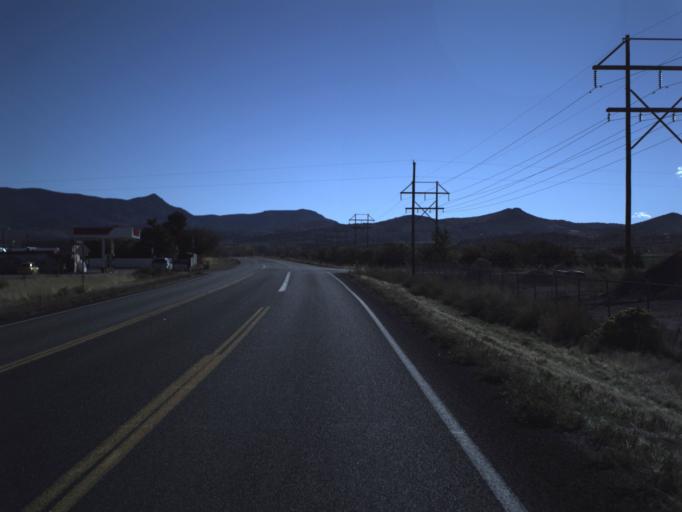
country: US
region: Utah
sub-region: Washington County
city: Enterprise
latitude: 37.6722
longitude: -113.5502
